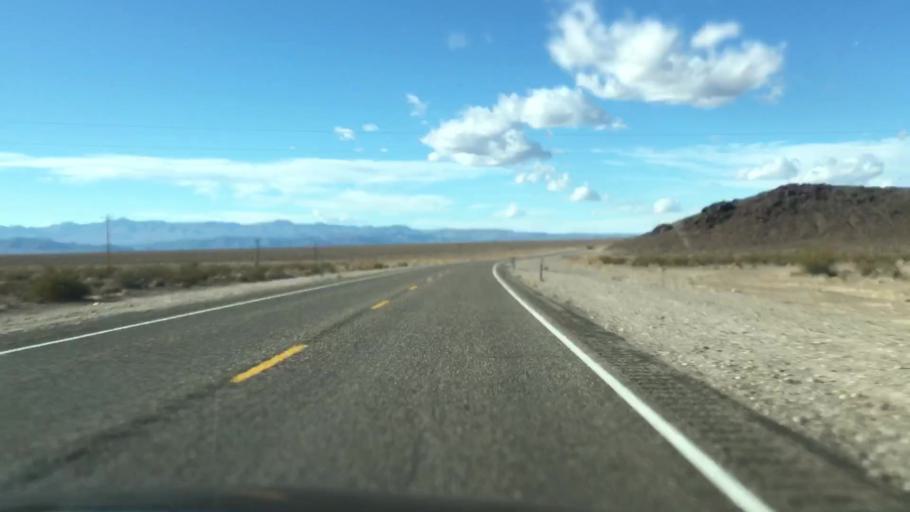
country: US
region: Nevada
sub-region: Nye County
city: Beatty
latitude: 37.1786
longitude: -116.9290
